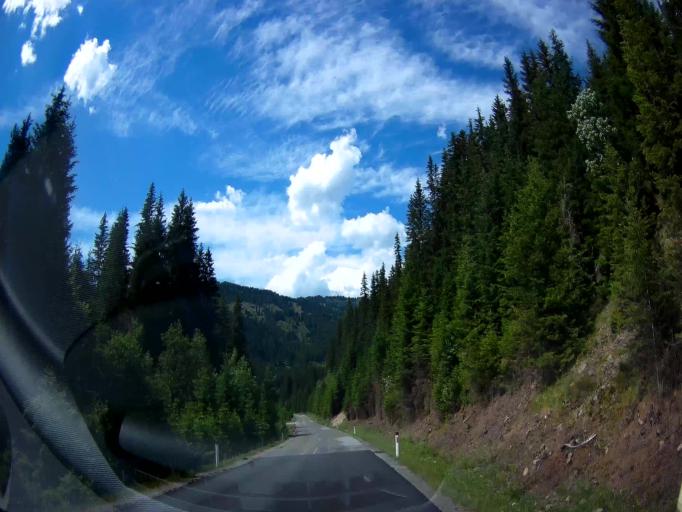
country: AT
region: Styria
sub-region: Politischer Bezirk Murau
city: Stadl an der Mur
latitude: 46.9734
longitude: 14.0111
